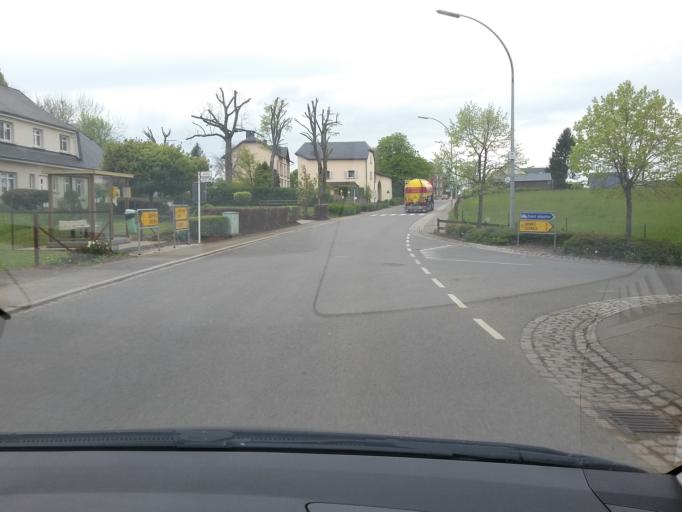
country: LU
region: Luxembourg
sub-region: Canton de Capellen
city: Garnich
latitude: 49.6034
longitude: 5.9271
